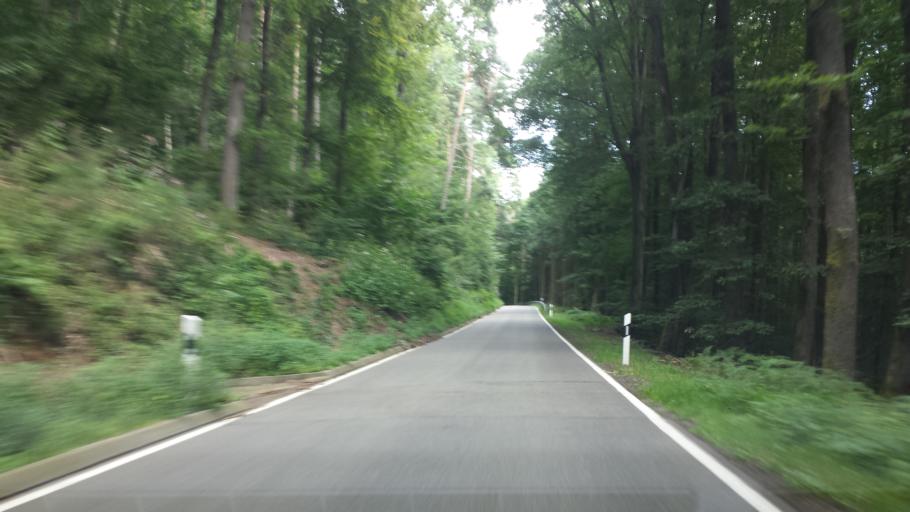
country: DE
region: Rheinland-Pfalz
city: Ramberg
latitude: 49.2723
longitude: 8.0168
